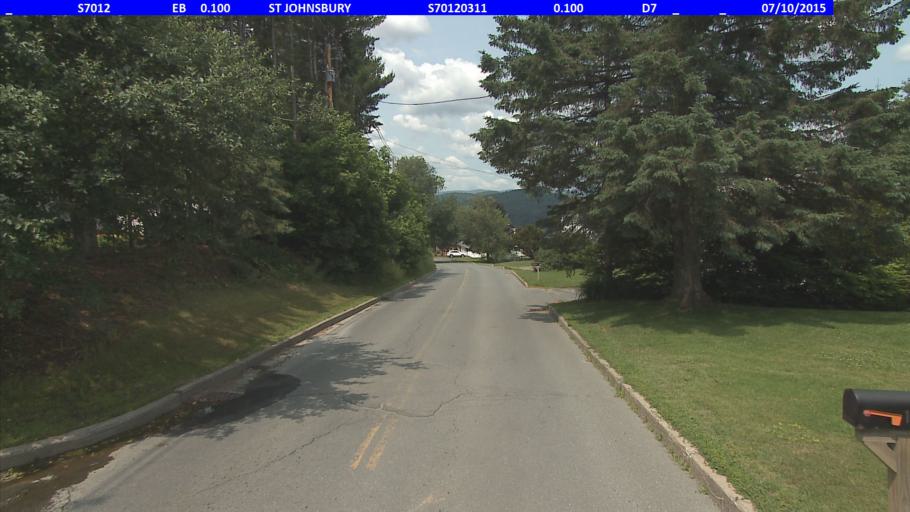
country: US
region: Vermont
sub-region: Caledonia County
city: Saint Johnsbury
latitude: 44.4174
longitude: -71.9937
